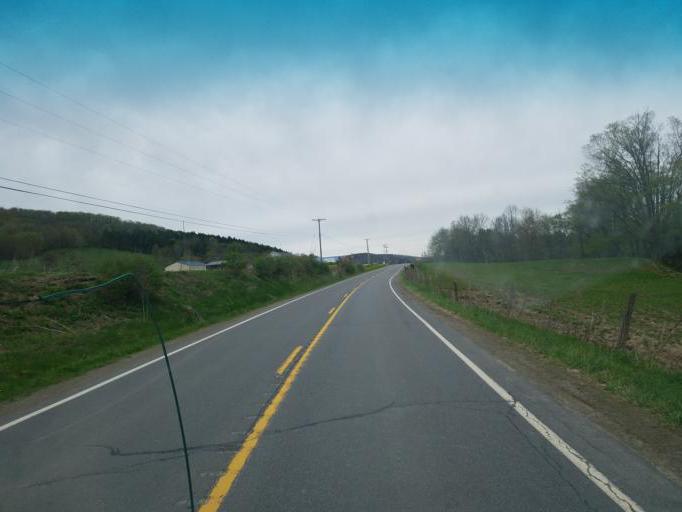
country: US
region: Pennsylvania
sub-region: Tioga County
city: Westfield
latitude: 41.8943
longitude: -77.5322
